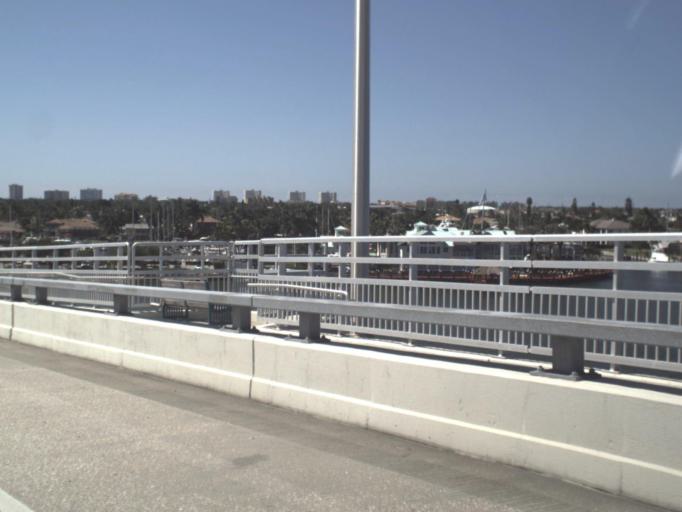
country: US
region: Florida
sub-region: Collier County
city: Marco
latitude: 25.9629
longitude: -81.7102
